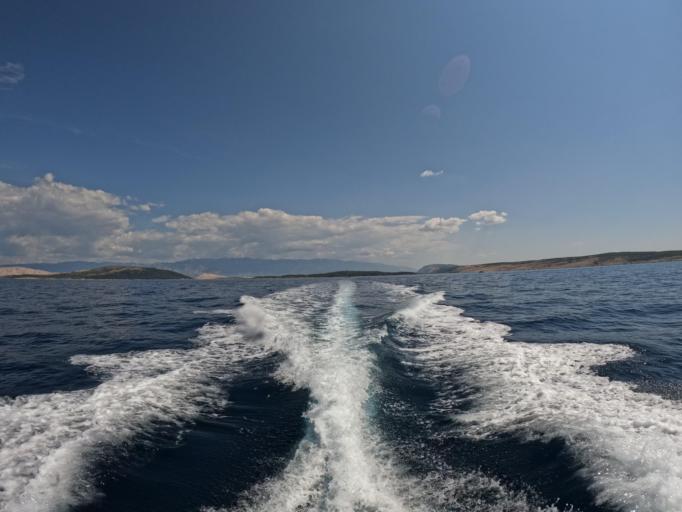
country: HR
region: Primorsko-Goranska
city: Lopar
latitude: 44.8618
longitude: 14.6925
